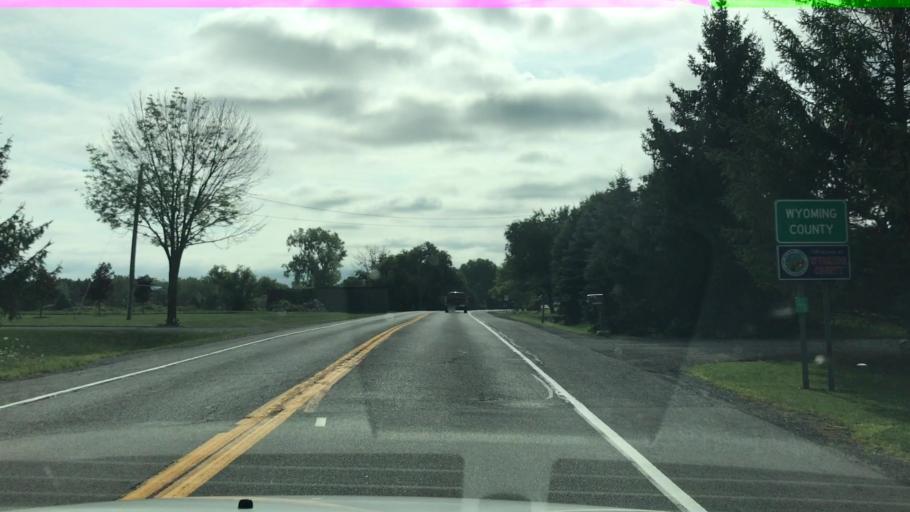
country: US
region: New York
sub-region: Erie County
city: Alden
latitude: 42.8497
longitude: -78.4868
